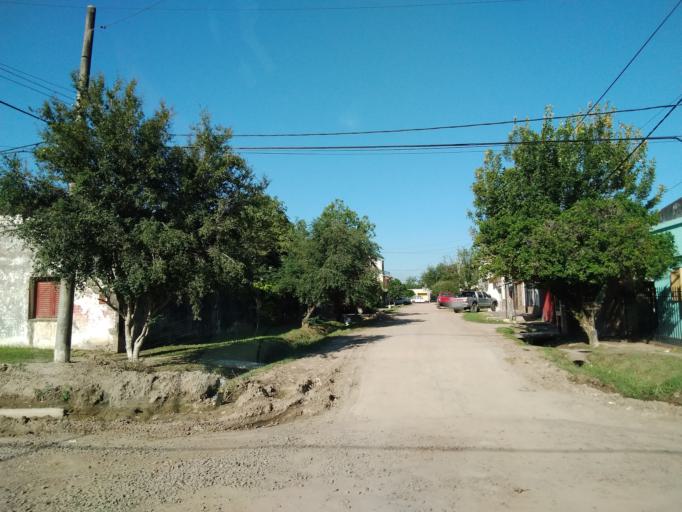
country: AR
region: Corrientes
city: Corrientes
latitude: -27.4808
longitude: -58.8124
